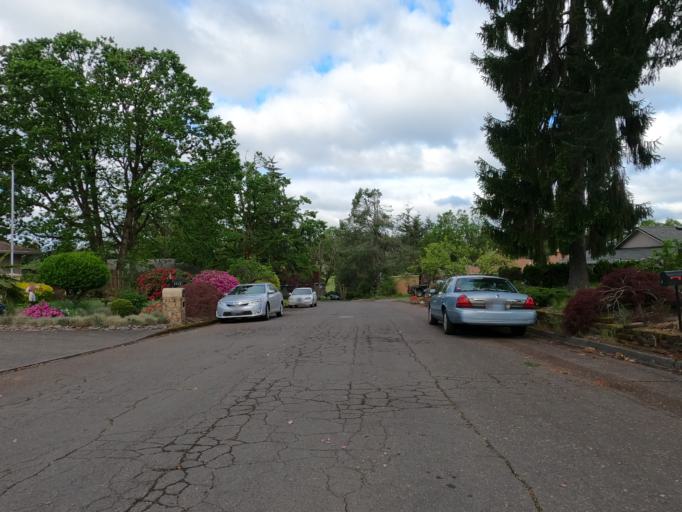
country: US
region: Oregon
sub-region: Clackamas County
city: Clackamas
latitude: 45.3959
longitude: -122.5832
